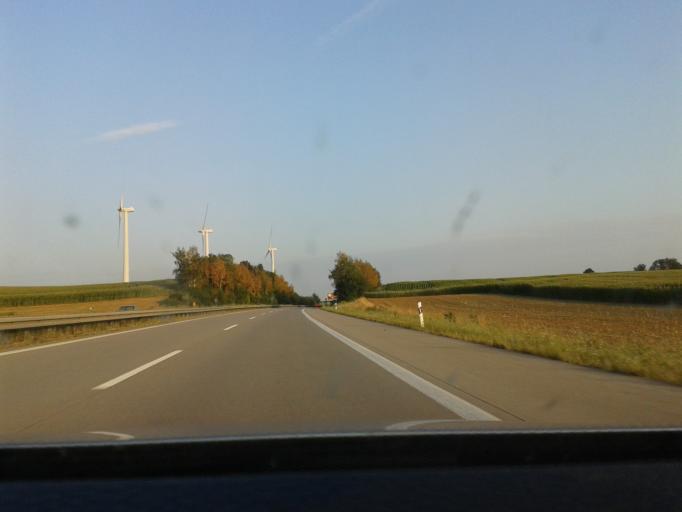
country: DE
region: Saxony
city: Mochau
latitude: 51.1319
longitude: 13.1628
